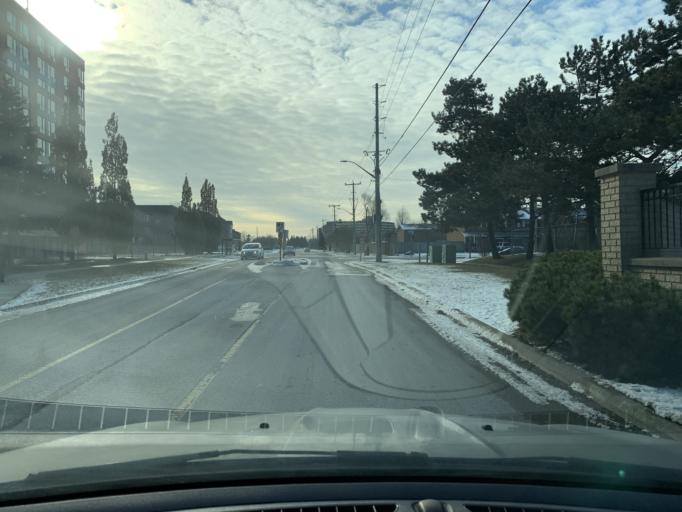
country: CA
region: Ontario
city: Etobicoke
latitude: 43.7195
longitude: -79.6251
